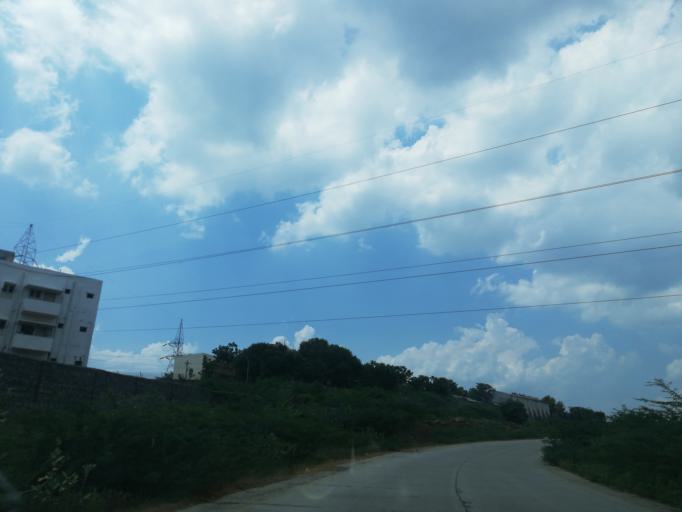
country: IN
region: Andhra Pradesh
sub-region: Guntur
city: Macherla
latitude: 16.5835
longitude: 79.3273
